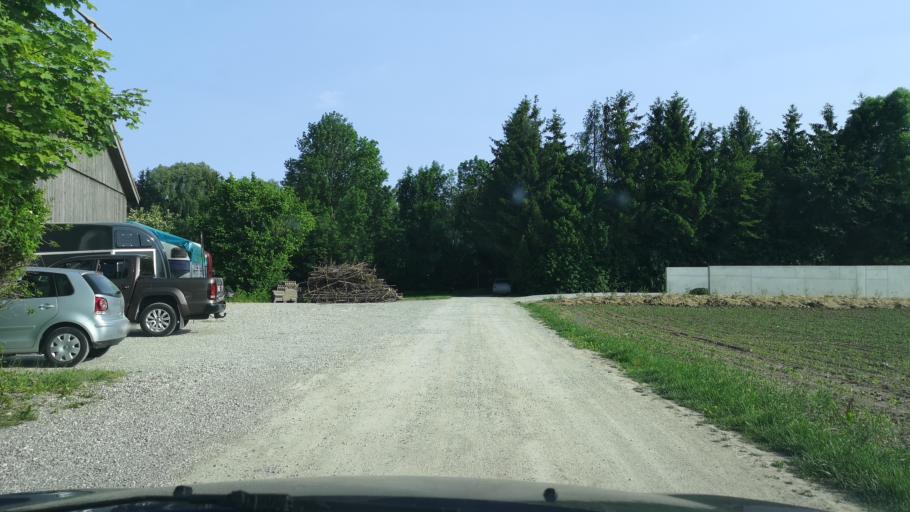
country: DE
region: Bavaria
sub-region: Upper Bavaria
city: Poing
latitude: 48.1760
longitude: 11.8216
